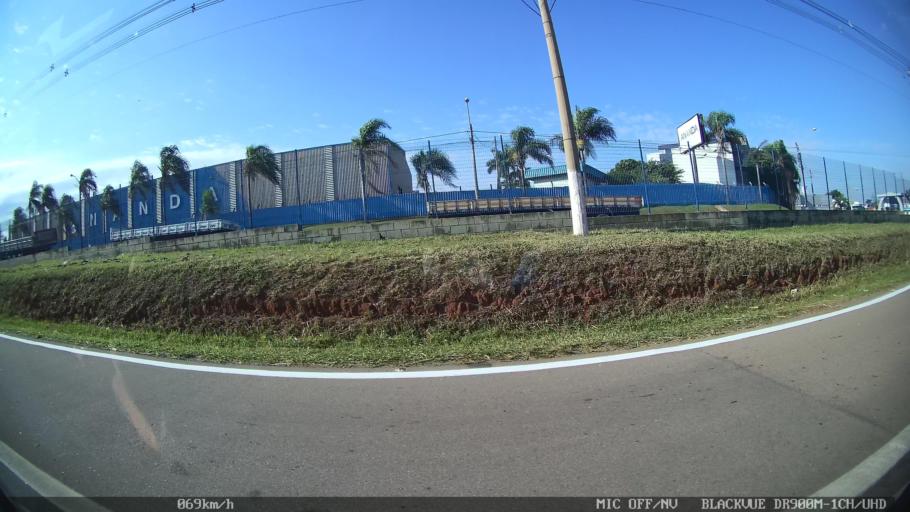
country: BR
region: Sao Paulo
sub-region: Piracicaba
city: Piracicaba
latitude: -22.6641
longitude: -47.6077
